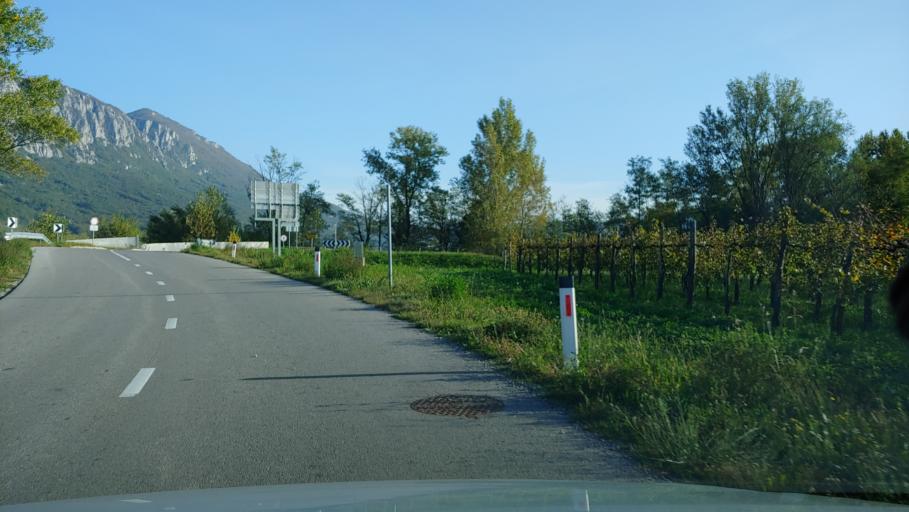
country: SI
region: Vipava
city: Vipava
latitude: 45.8360
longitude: 13.9493
